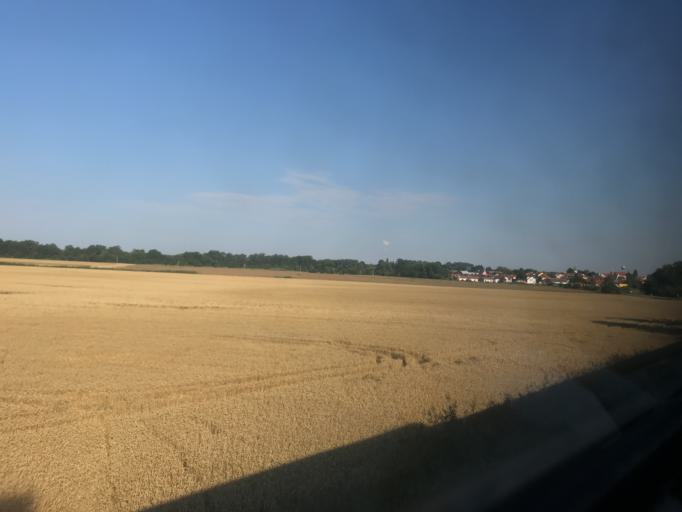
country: CZ
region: Jihocesky
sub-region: Okres Jindrichuv Hradec
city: Lomnice nad Luznici
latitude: 49.0749
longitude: 14.7288
